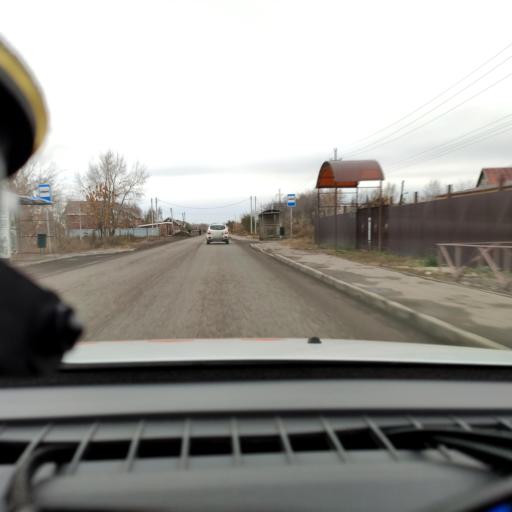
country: RU
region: Samara
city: Samara
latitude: 53.1290
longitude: 50.2365
